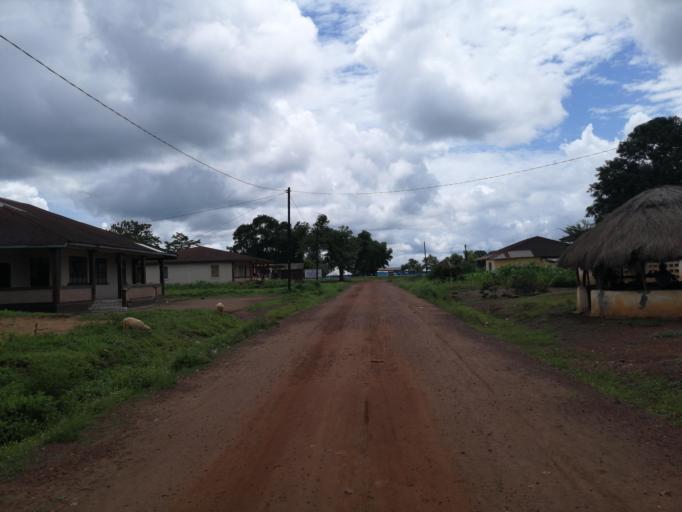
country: SL
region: Northern Province
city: Port Loko
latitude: 8.7738
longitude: -12.7905
